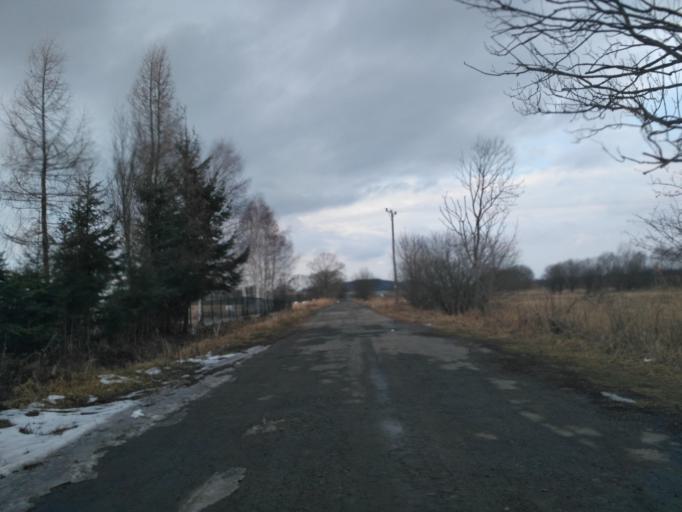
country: PL
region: Subcarpathian Voivodeship
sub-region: Powiat sanocki
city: Strachocina
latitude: 49.6030
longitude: 22.1348
